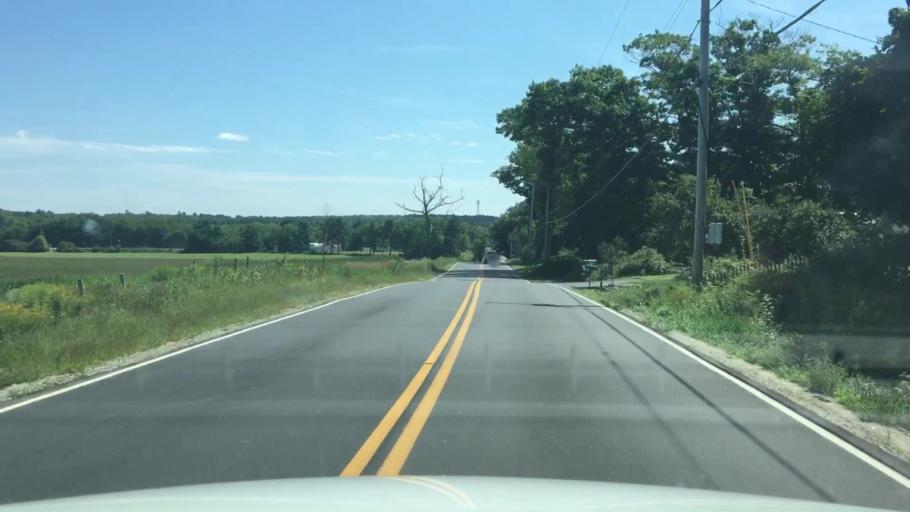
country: US
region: Maine
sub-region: Sagadahoc County
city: Topsham
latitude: 43.9582
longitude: -69.9756
